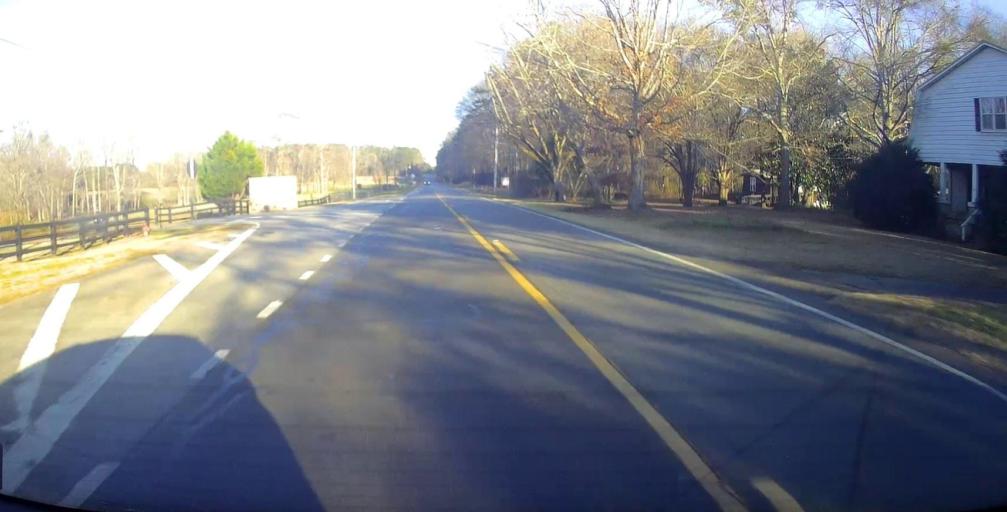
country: US
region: Georgia
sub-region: Harris County
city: Pine Mountain
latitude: 32.8525
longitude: -84.8631
